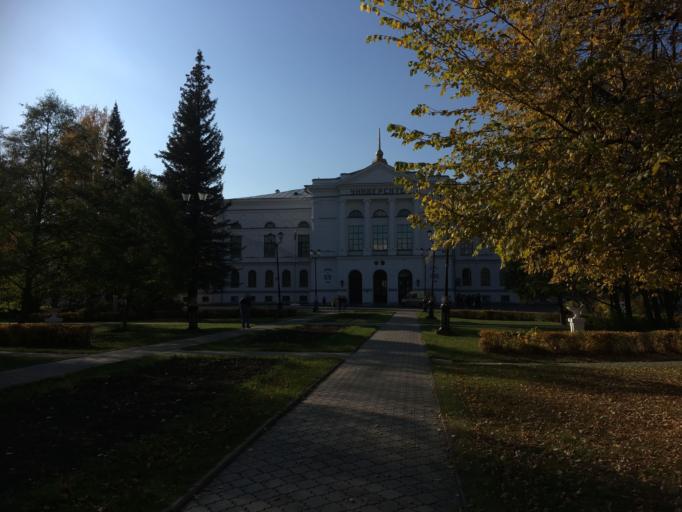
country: RU
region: Tomsk
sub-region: Tomskiy Rayon
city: Tomsk
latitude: 56.4695
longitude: 84.9498
